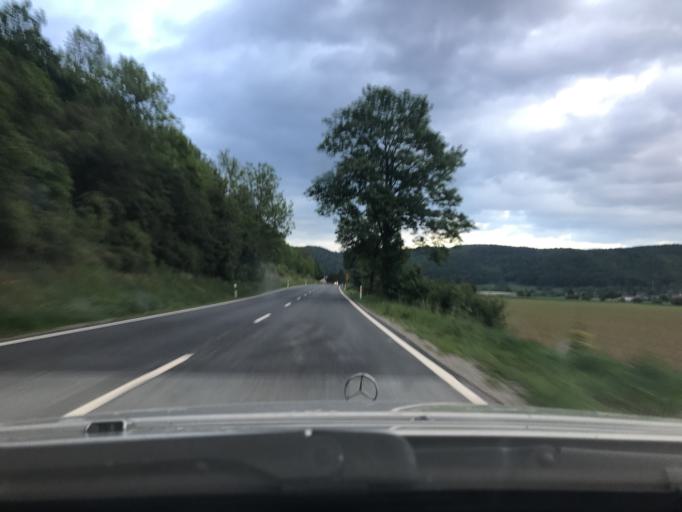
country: DE
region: Thuringia
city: Kella
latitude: 51.1929
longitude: 10.1167
